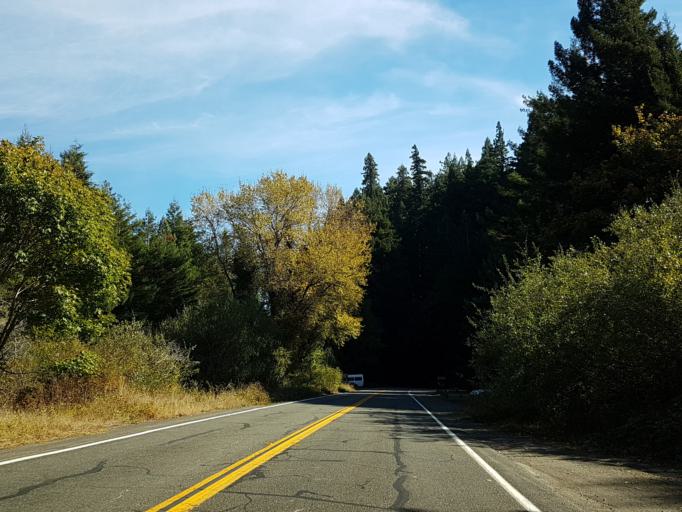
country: US
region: California
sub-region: Humboldt County
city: Rio Dell
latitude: 40.4441
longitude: -123.9870
